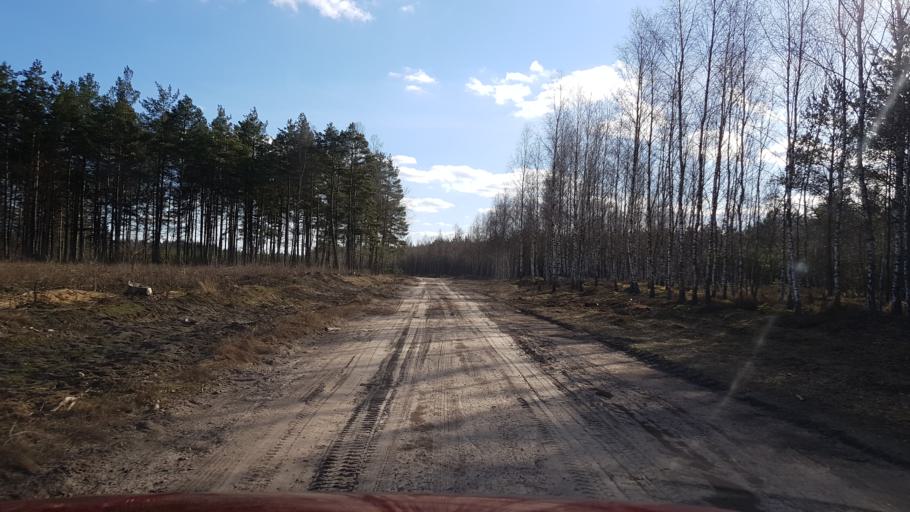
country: PL
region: Greater Poland Voivodeship
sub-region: Powiat zlotowski
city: Sypniewo
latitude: 53.5346
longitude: 16.6463
